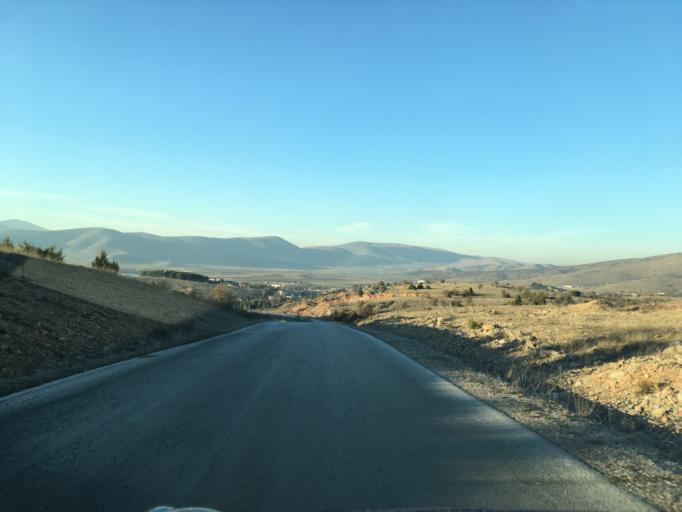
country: GR
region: West Macedonia
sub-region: Nomos Kozanis
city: Kozani
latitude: 40.2766
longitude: 21.7347
